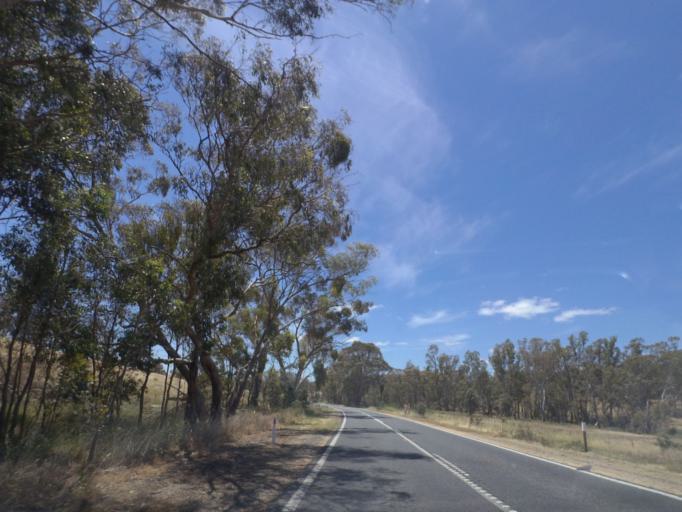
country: AU
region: Victoria
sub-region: Mount Alexander
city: Castlemaine
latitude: -37.2001
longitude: 144.1454
